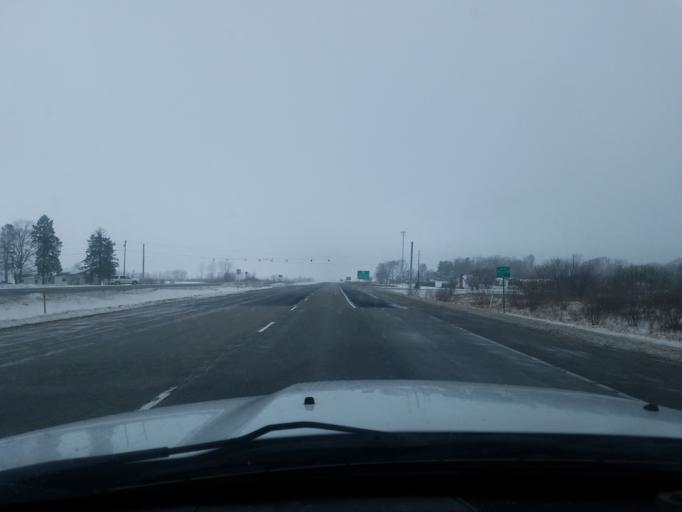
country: US
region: Indiana
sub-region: Fulton County
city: Rochester
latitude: 41.0417
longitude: -86.2009
